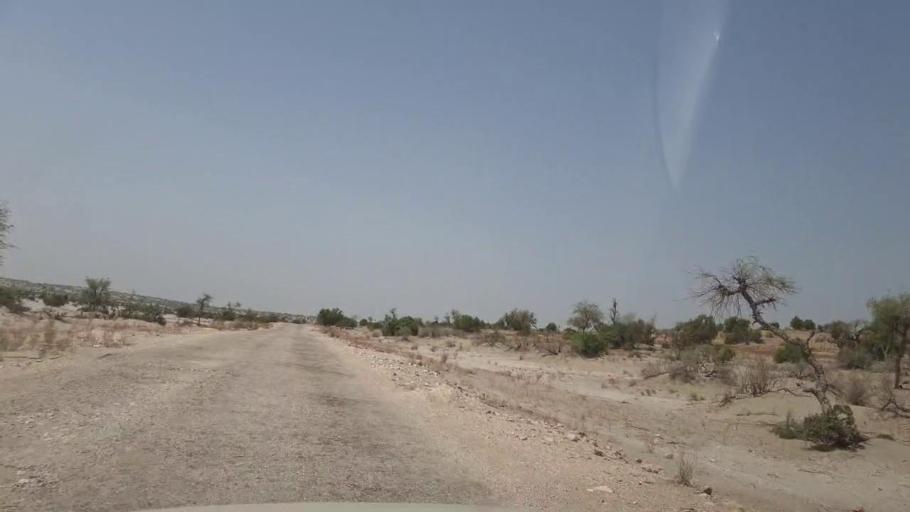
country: PK
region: Sindh
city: Khanpur
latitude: 27.3436
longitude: 69.3175
